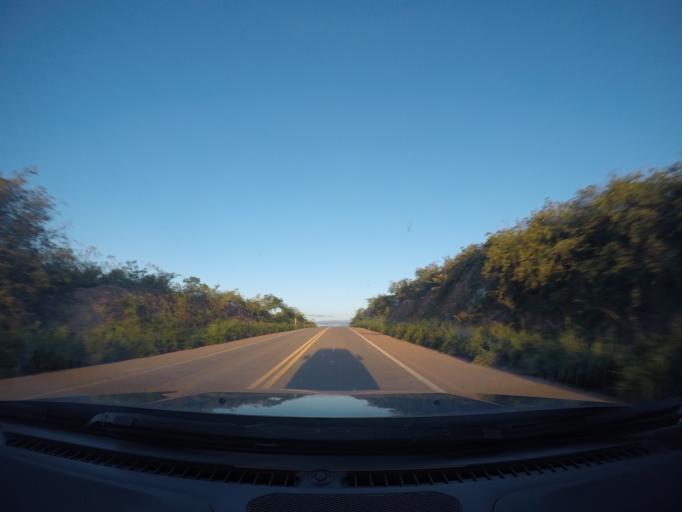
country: BR
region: Bahia
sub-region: Seabra
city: Seabra
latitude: -12.3954
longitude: -41.9309
